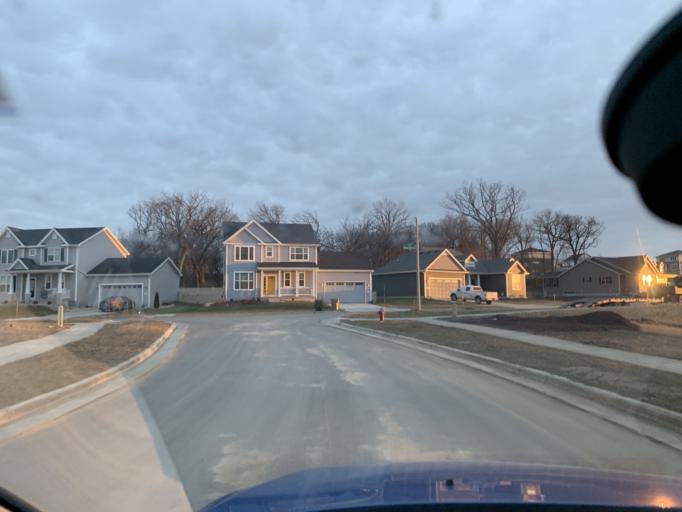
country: US
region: Wisconsin
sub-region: Dane County
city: Verona
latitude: 43.0496
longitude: -89.5595
